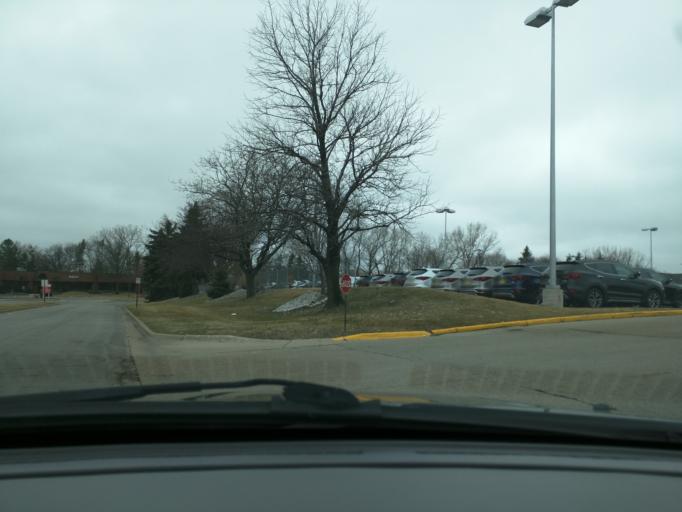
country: US
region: Minnesota
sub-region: Hennepin County
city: Edina
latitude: 44.8573
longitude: -93.3407
